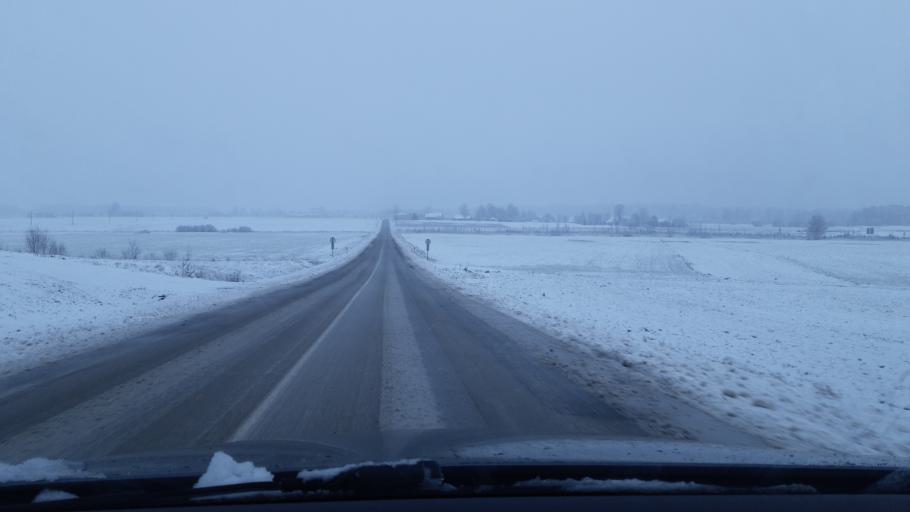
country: LT
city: Kaisiadorys
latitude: 54.8538
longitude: 24.3578
